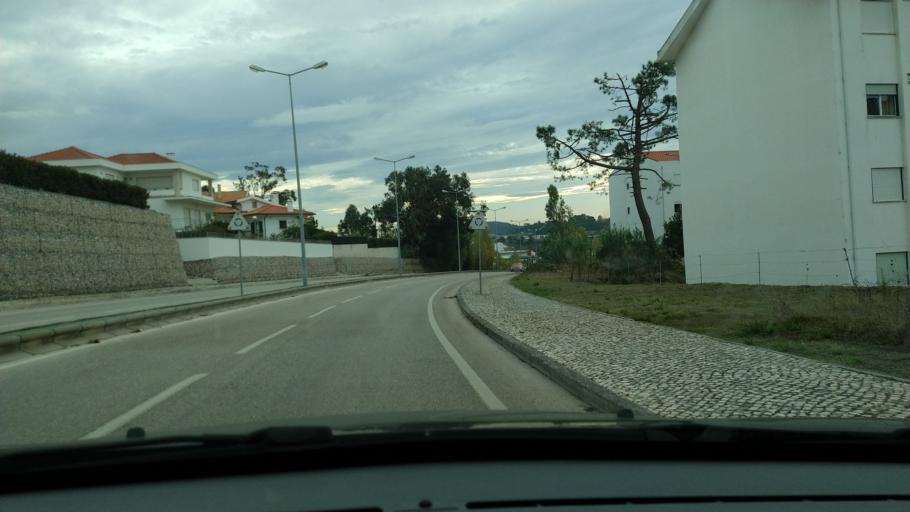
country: PT
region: Coimbra
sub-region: Figueira da Foz
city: Figueira da Foz
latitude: 40.1584
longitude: -8.8516
